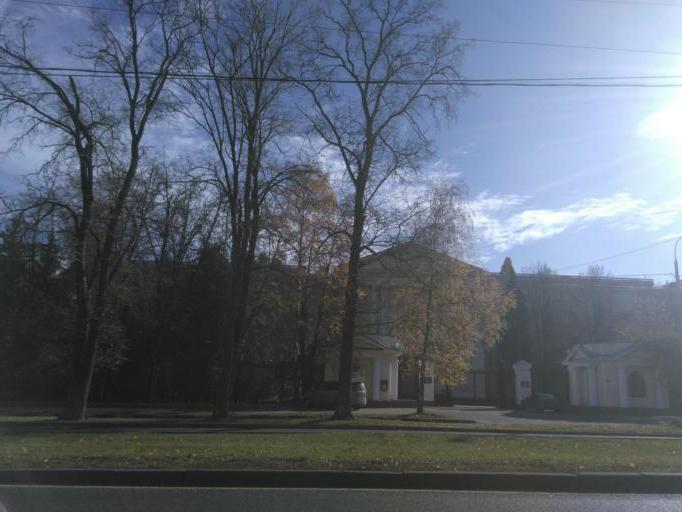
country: RU
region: Moskovskaya
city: Leninskiye Gory
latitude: 55.7010
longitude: 37.5684
